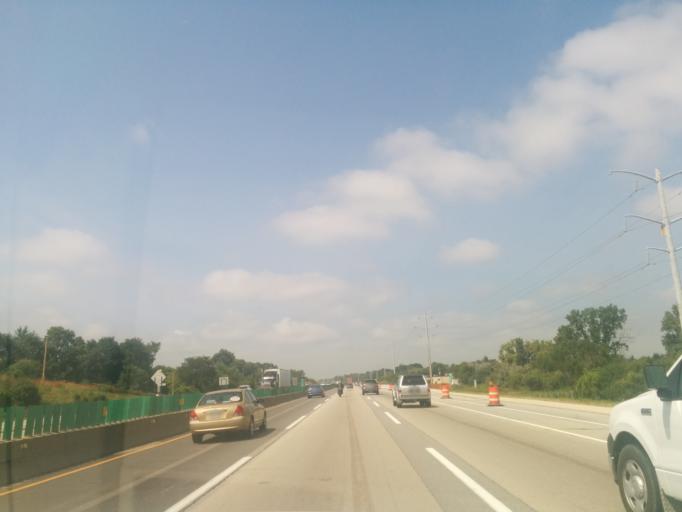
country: US
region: Illinois
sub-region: Cook County
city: Hoffman Estates
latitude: 42.0651
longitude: -88.0894
